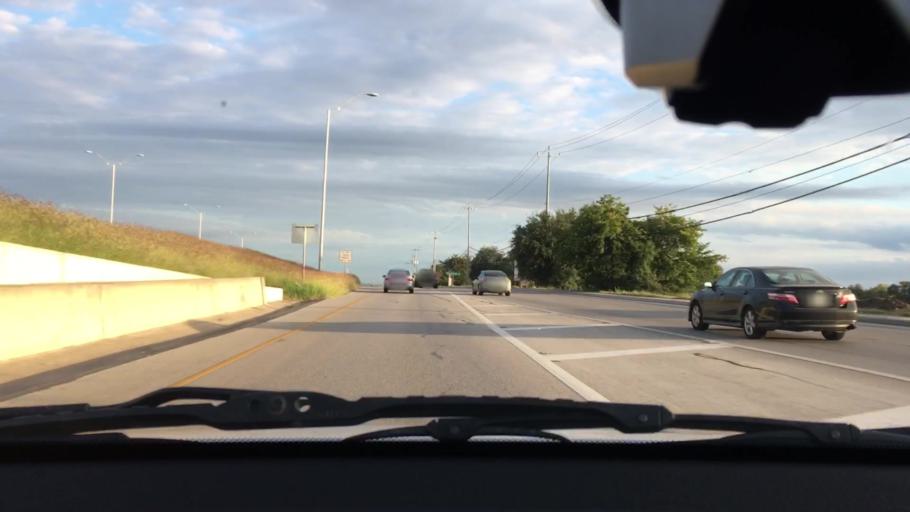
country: US
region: Texas
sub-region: Bexar County
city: Live Oak
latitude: 29.5556
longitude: -98.3243
